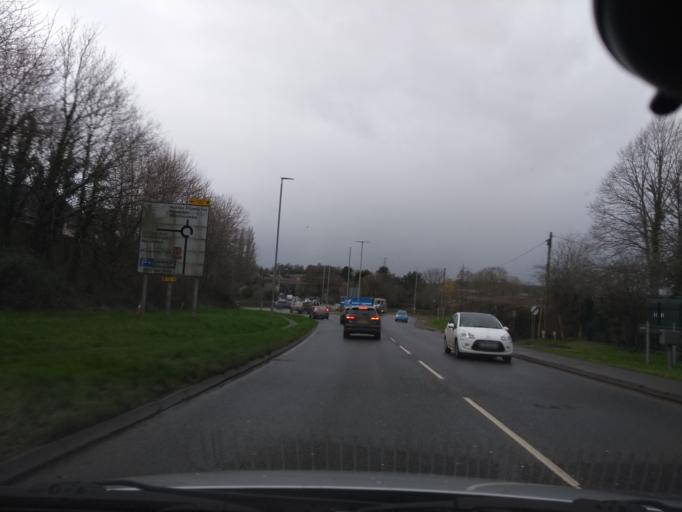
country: GB
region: England
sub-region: Somerset
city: Taunton
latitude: 51.0310
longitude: -3.1321
